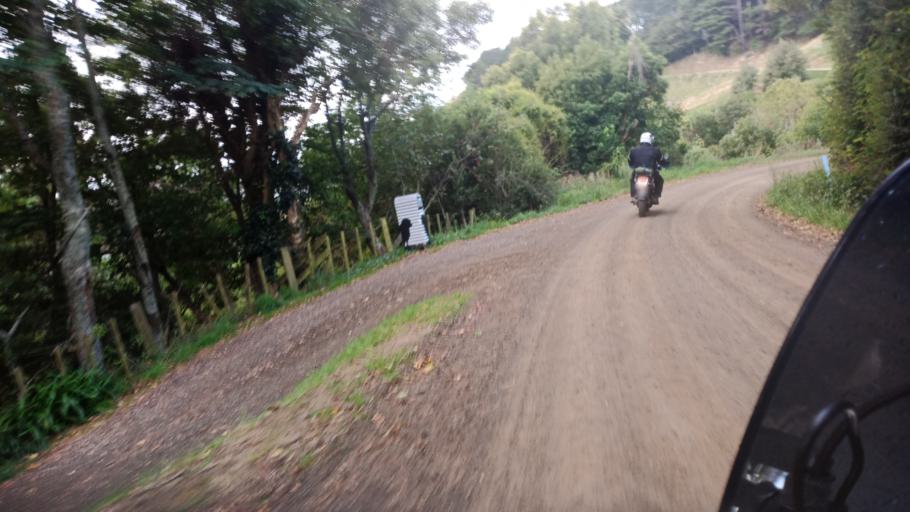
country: NZ
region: Gisborne
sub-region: Gisborne District
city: Gisborne
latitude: -38.4711
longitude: 177.6177
